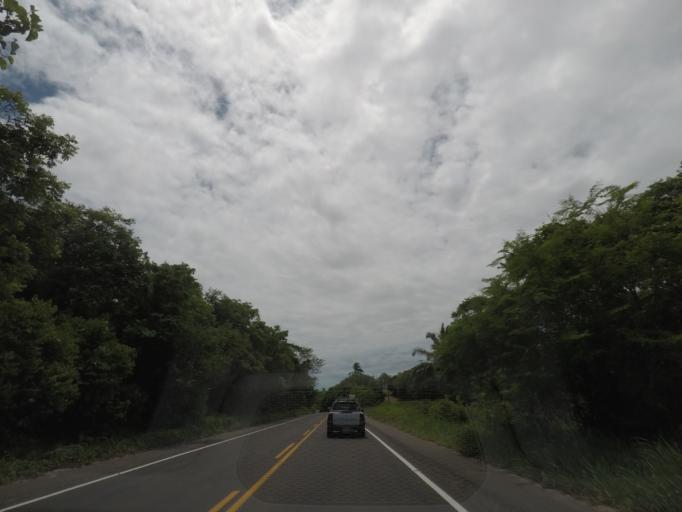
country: BR
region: Bahia
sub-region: Itaparica
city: Itaparica
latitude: -12.9641
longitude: -38.6350
